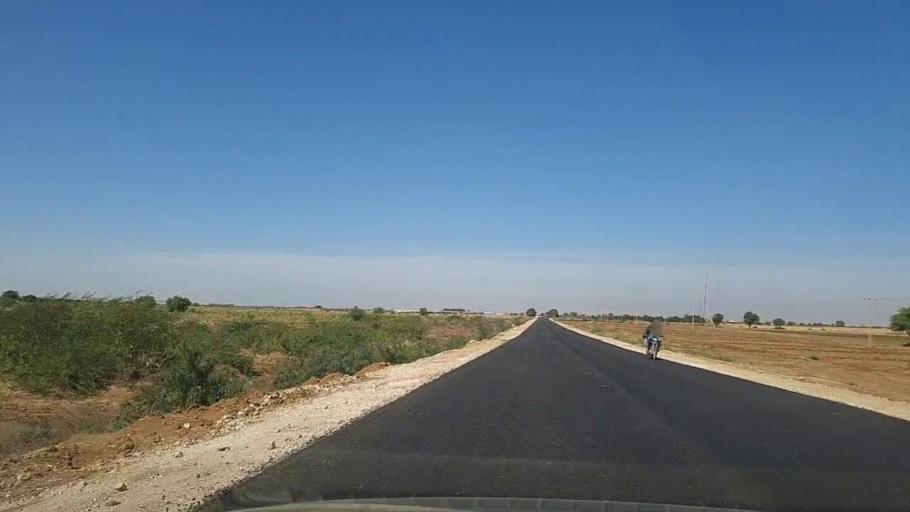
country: PK
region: Sindh
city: Kotri
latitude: 25.2439
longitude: 68.2300
